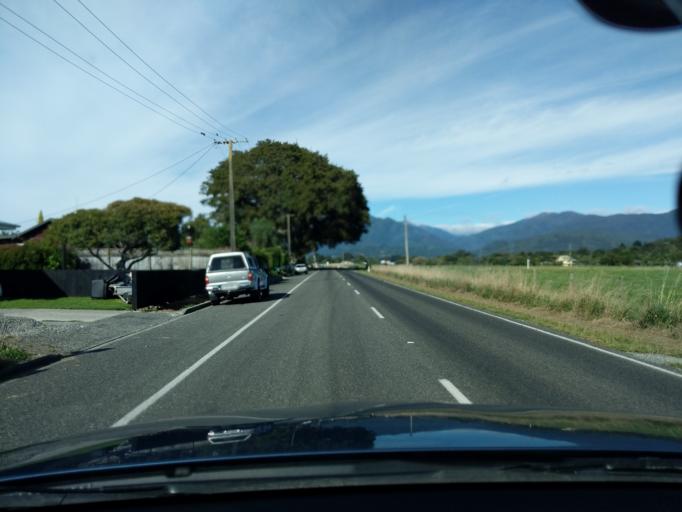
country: NZ
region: Tasman
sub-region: Tasman District
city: Takaka
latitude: -40.8509
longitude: 172.8310
